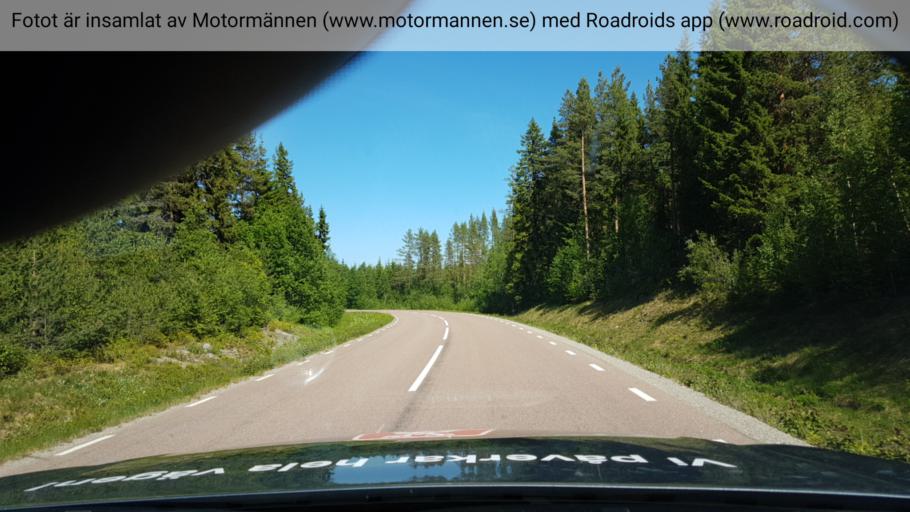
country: SE
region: Jaemtland
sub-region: Braecke Kommun
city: Braecke
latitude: 62.7510
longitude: 15.2747
